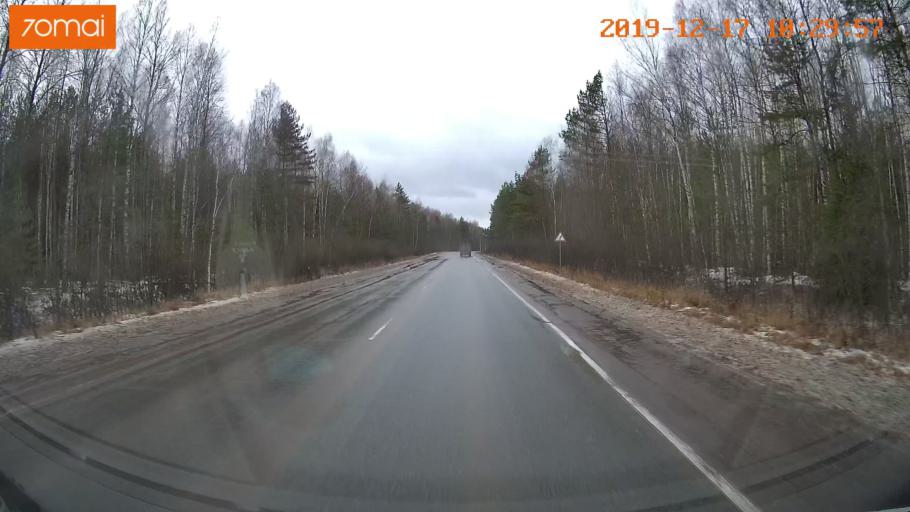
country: RU
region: Vladimir
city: Anopino
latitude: 55.6467
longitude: 40.7143
